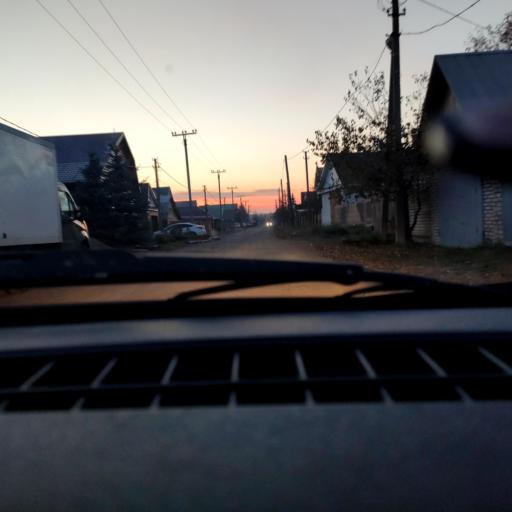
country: RU
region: Bashkortostan
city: Iglino
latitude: 54.8356
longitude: 56.1811
